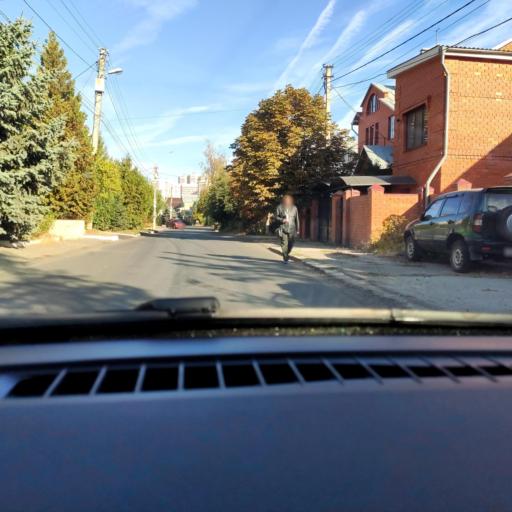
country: RU
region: Voronezj
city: Voronezh
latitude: 51.7041
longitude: 39.2045
